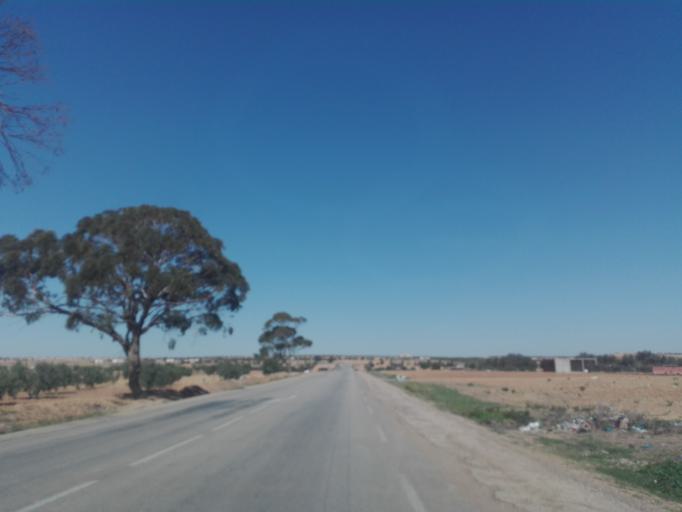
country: TN
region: Safaqis
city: Bi'r `Ali Bin Khalifah
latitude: 34.7431
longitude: 10.3666
